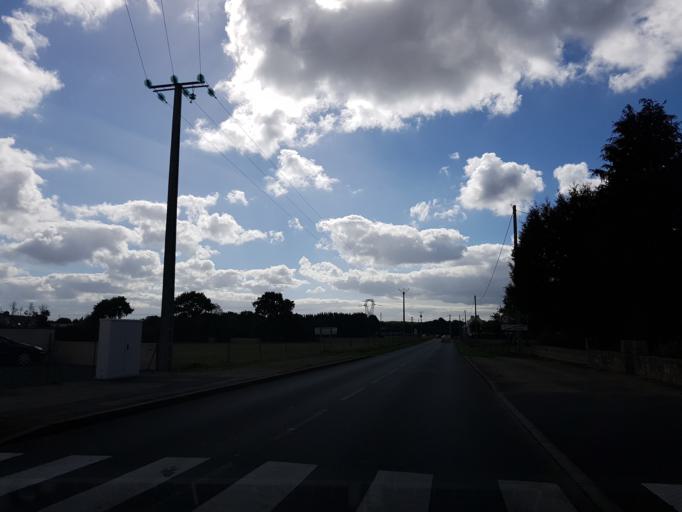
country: FR
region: Brittany
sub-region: Departement des Cotes-d'Armor
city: Yffiniac
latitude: 48.4702
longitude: -2.6941
